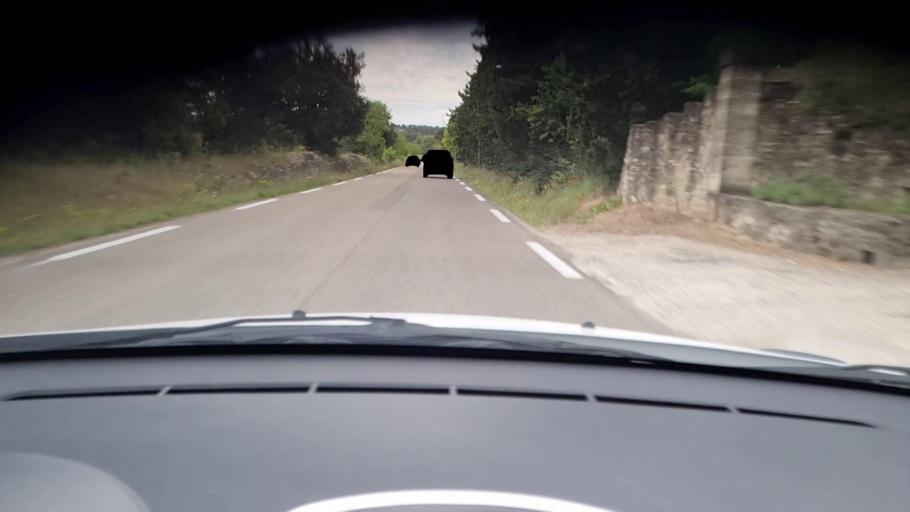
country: FR
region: Languedoc-Roussillon
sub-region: Departement du Gard
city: Uzes
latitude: 43.9895
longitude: 4.4120
